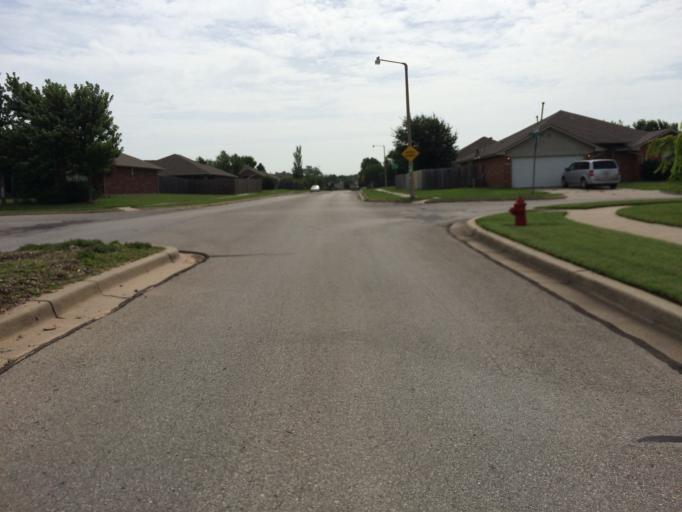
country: US
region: Oklahoma
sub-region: Cleveland County
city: Norman
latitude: 35.1986
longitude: -97.4233
